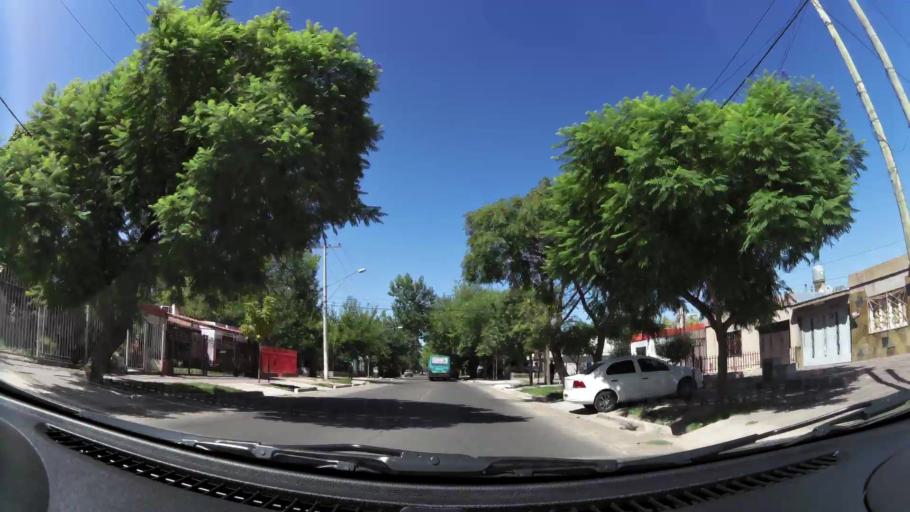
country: AR
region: Mendoza
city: Mendoza
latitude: -32.8856
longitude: -68.8075
